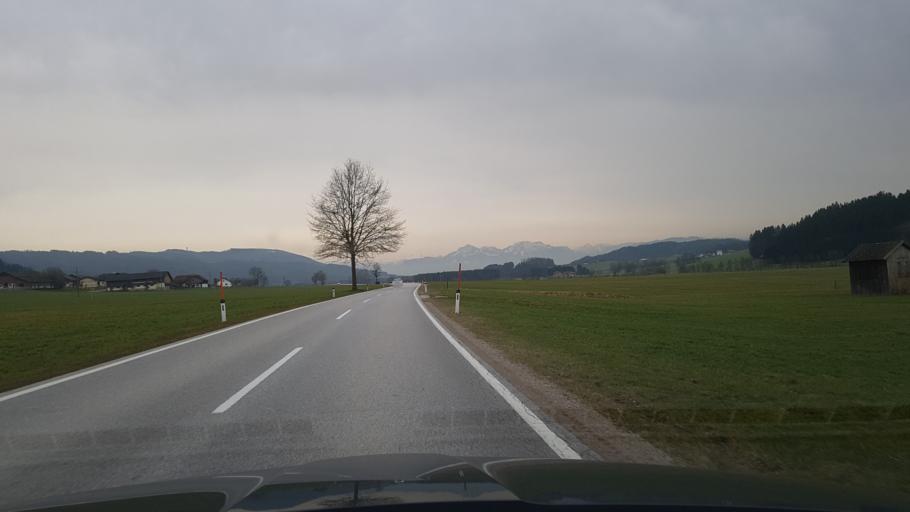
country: AT
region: Salzburg
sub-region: Politischer Bezirk Salzburg-Umgebung
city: Nussdorf am Haunsberg
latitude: 47.9797
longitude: 13.0114
